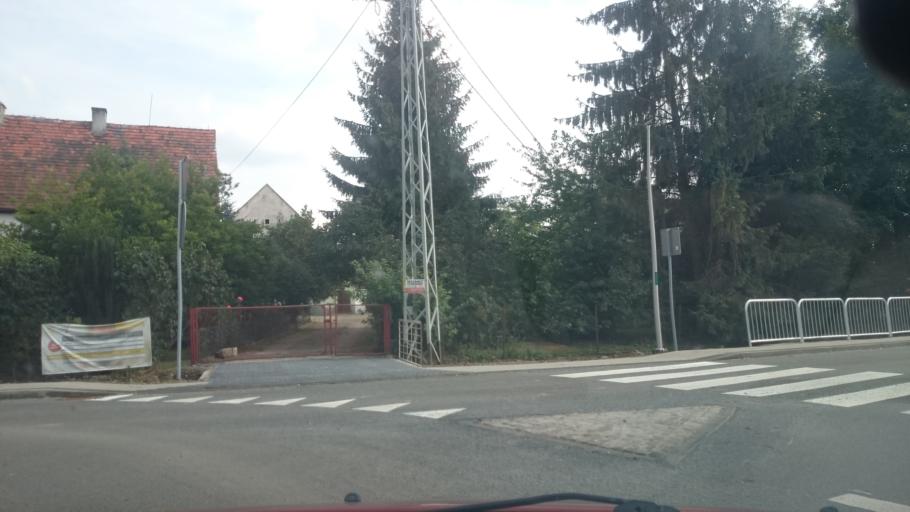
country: PL
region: Opole Voivodeship
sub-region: Powiat nyski
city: Otmuchow
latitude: 50.4991
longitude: 17.2185
